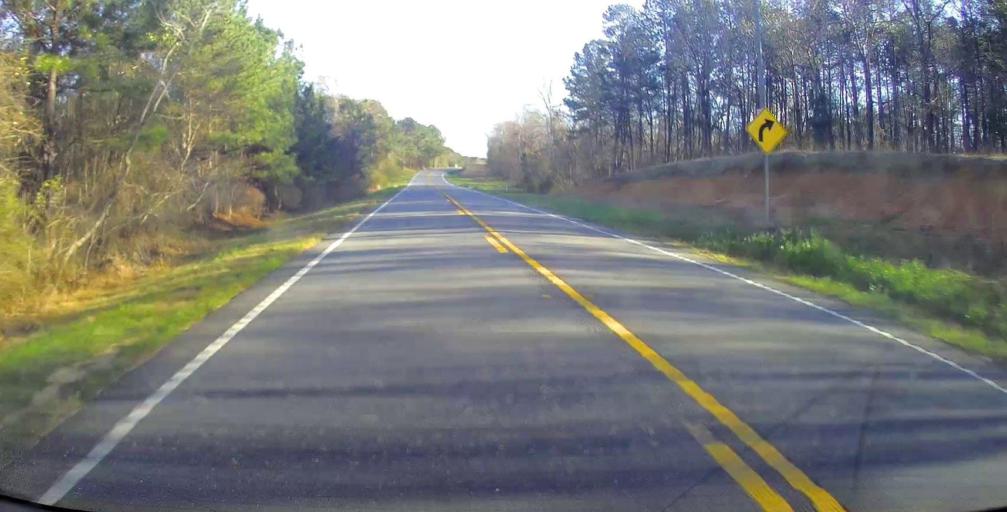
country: US
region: Georgia
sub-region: Taylor County
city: Butler
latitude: 32.4910
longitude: -84.3986
